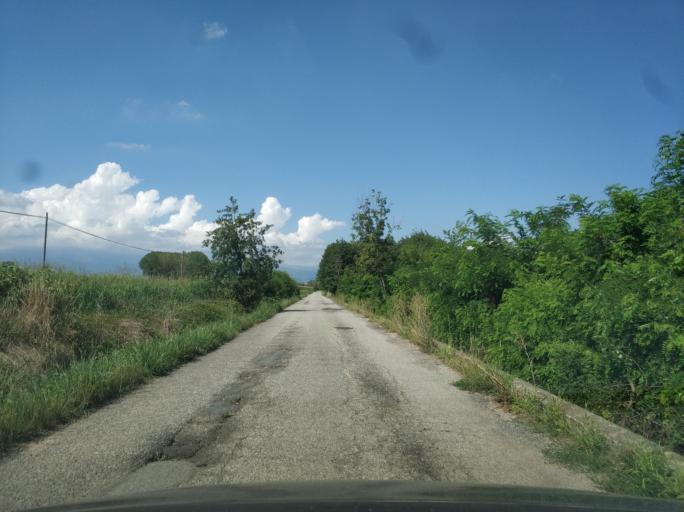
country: IT
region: Piedmont
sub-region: Provincia di Torino
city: Feletto
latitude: 45.3012
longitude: 7.7235
